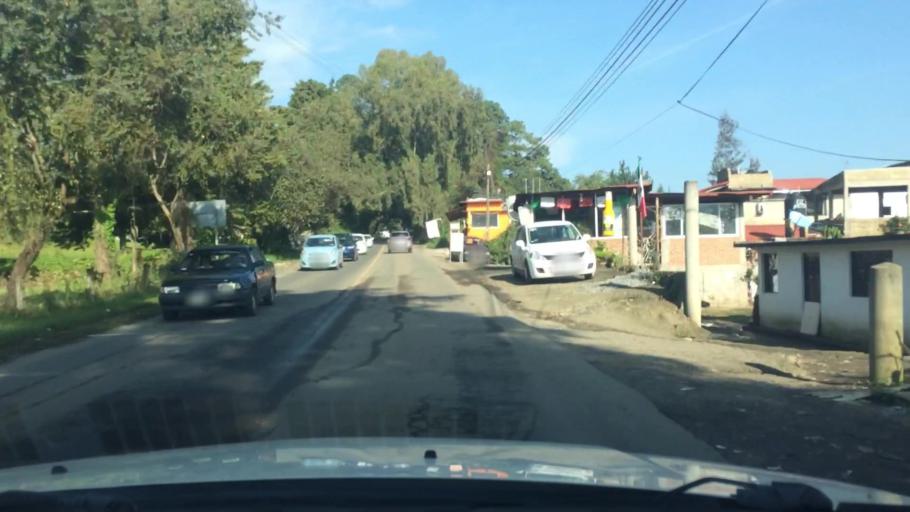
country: MX
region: Mexico
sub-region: Valle de Bravo
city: Cuadrilla de Dolores
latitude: 19.1480
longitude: -100.0714
